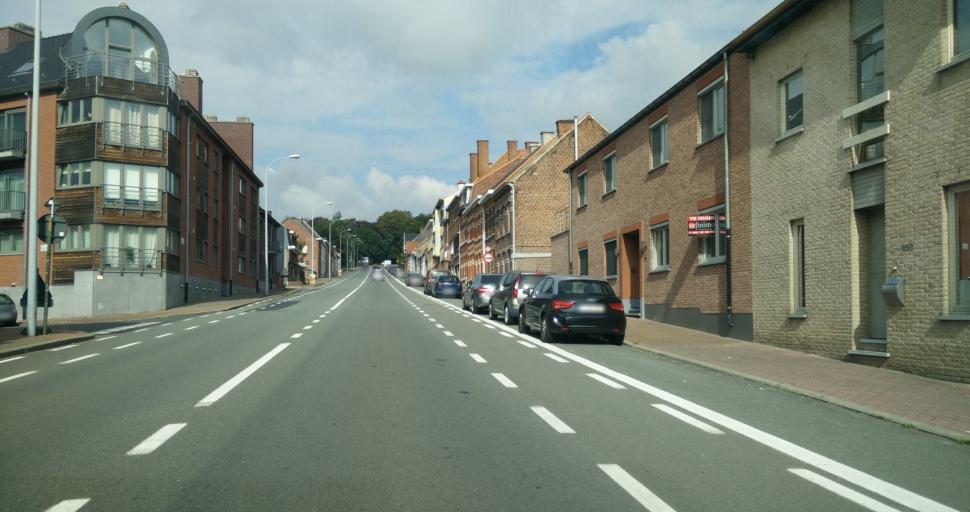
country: BE
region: Flanders
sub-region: Provincie Oost-Vlaanderen
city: Ronse
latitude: 50.7553
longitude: 3.5909
